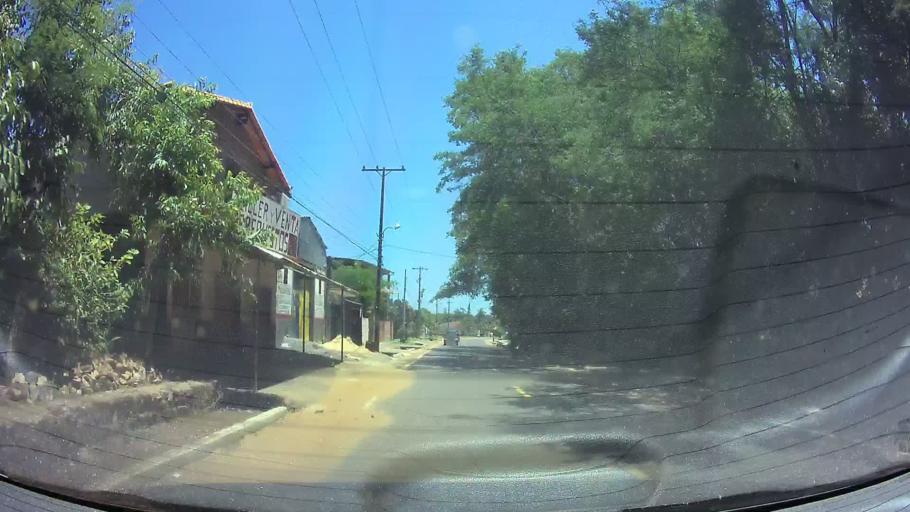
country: PY
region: Central
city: Limpio
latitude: -25.2502
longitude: -57.4904
